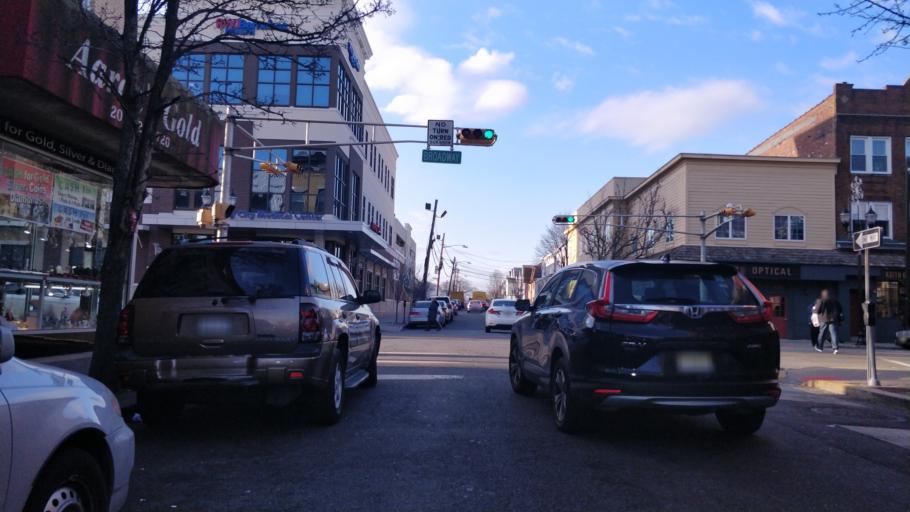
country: US
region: New Jersey
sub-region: Hudson County
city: Bayonne
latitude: 40.6647
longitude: -74.1173
